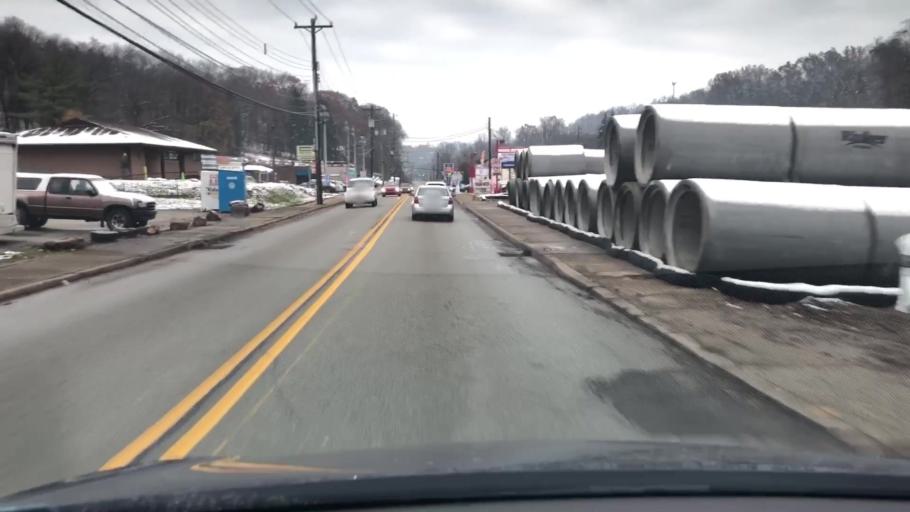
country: US
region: Pennsylvania
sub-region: Allegheny County
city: Churchill
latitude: 40.4516
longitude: -79.8266
